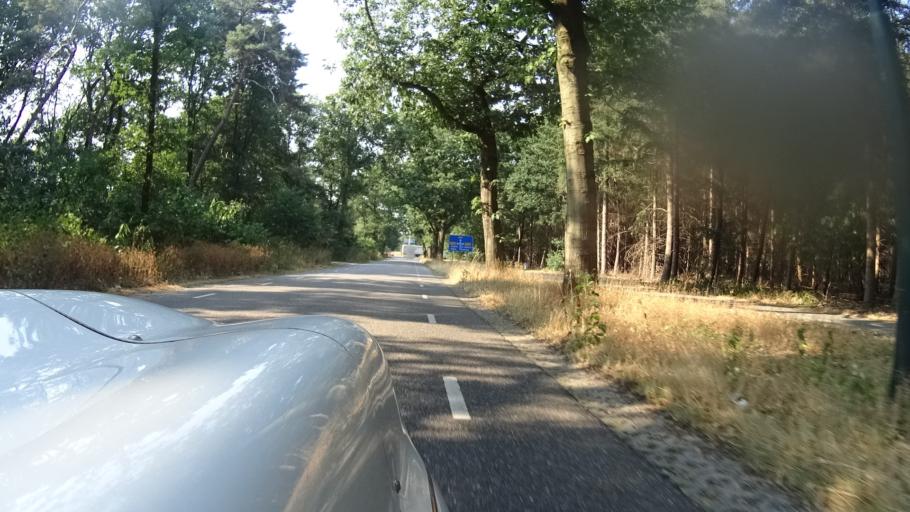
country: NL
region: North Brabant
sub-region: Gemeente Mill en Sint Hubert
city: Wilbertoord
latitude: 51.6697
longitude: 5.7726
